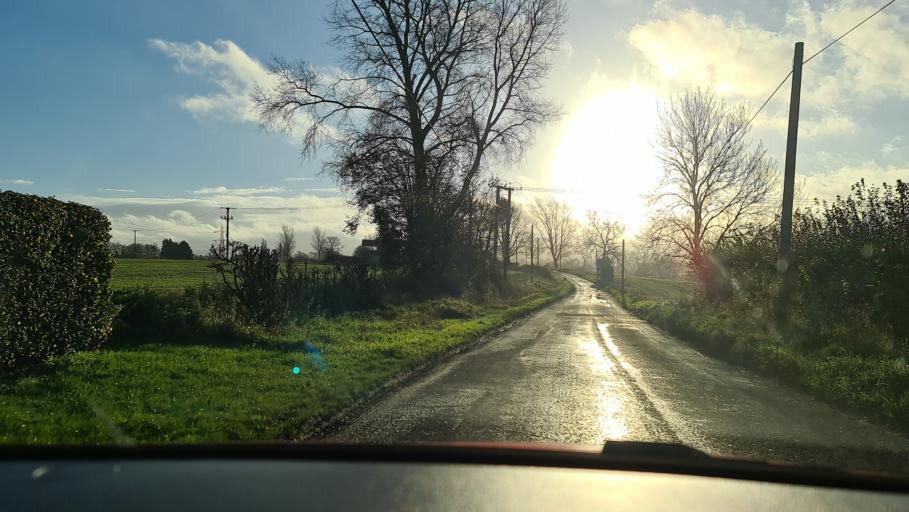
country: GB
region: England
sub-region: Buckinghamshire
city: Weston Turville
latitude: 51.7739
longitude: -0.7987
